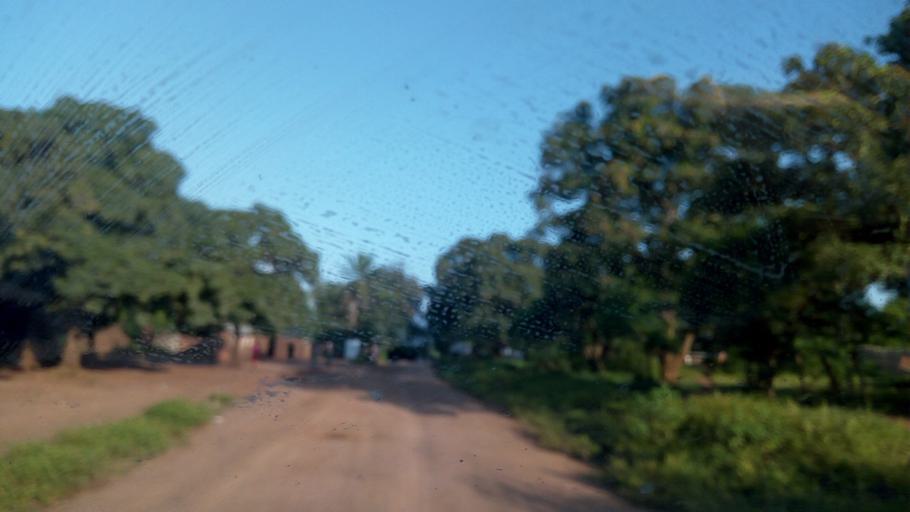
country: BI
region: Bururi
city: Rumonge
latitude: -4.2030
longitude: 29.0421
